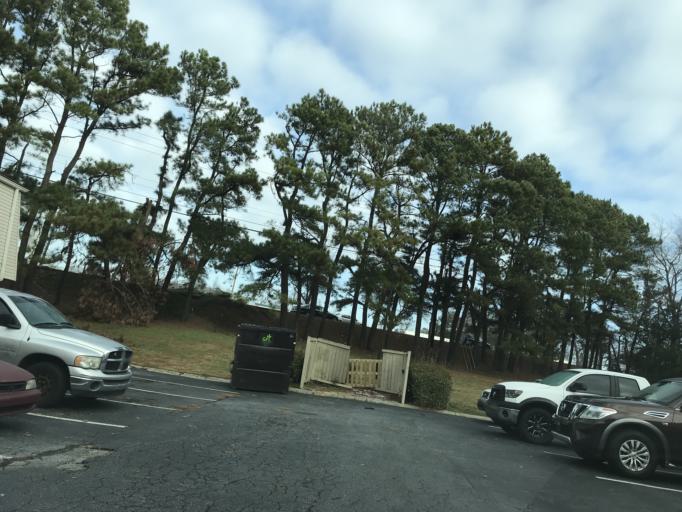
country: US
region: Georgia
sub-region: Clayton County
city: Riverdale
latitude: 33.5799
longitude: -84.3802
